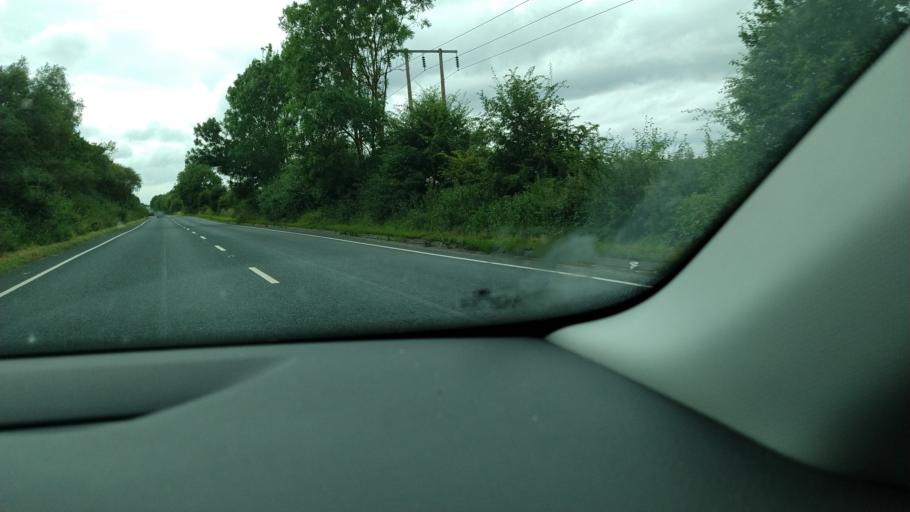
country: GB
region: England
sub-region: East Riding of Yorkshire
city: Rawcliffe
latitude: 53.7107
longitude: -0.9476
